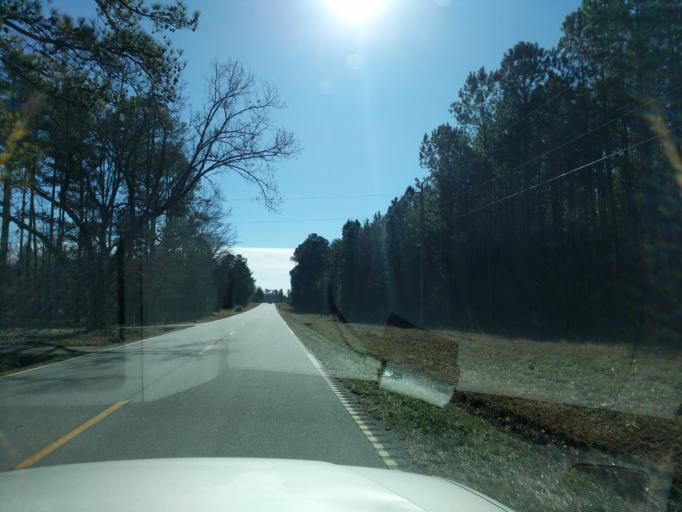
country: US
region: South Carolina
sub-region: Saluda County
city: Saluda
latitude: 34.0826
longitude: -81.8231
